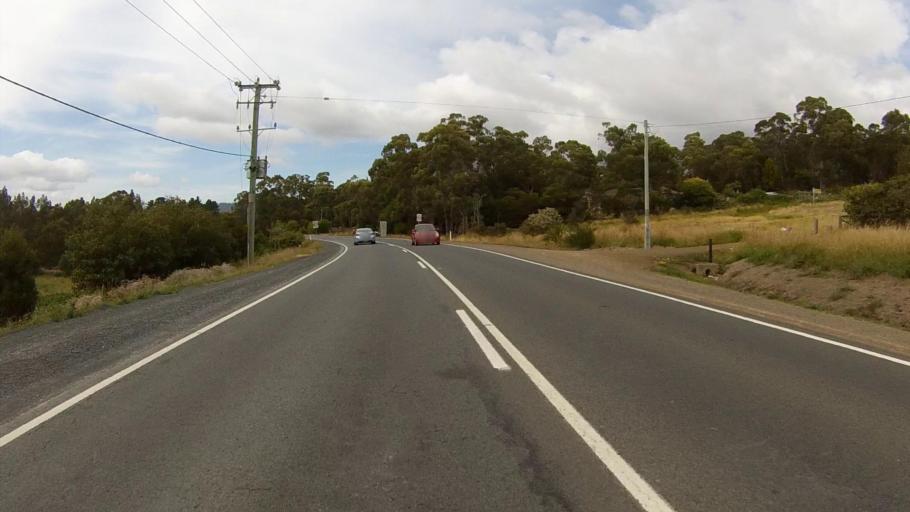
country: AU
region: Tasmania
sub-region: Kingborough
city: Margate
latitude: -43.0377
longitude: 147.2660
